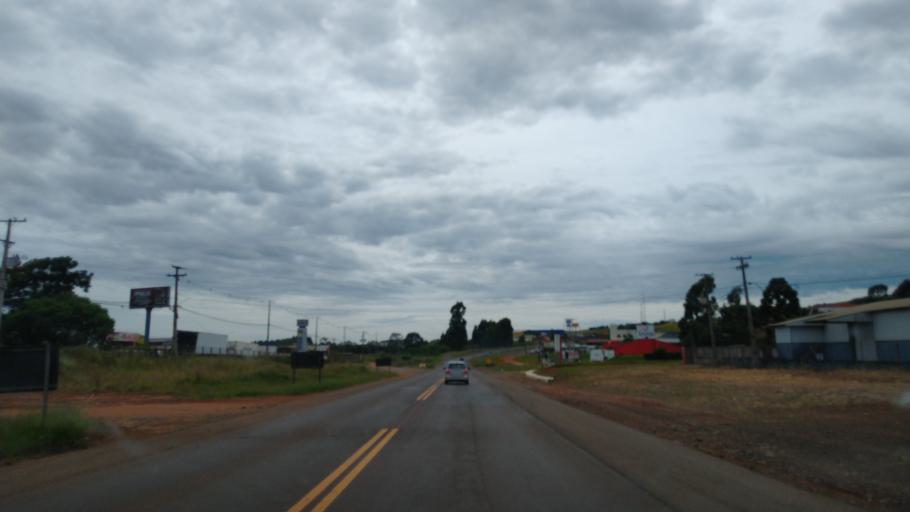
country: BR
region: Parana
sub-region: Pato Branco
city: Pato Branco
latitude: -26.2689
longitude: -52.7065
